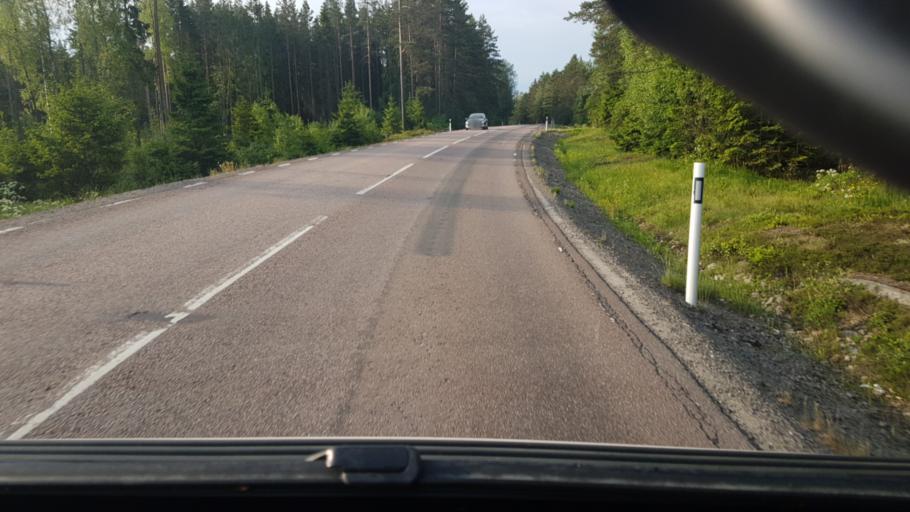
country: SE
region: Vaermland
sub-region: Eda Kommun
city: Charlottenberg
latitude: 59.8643
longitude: 12.2974
